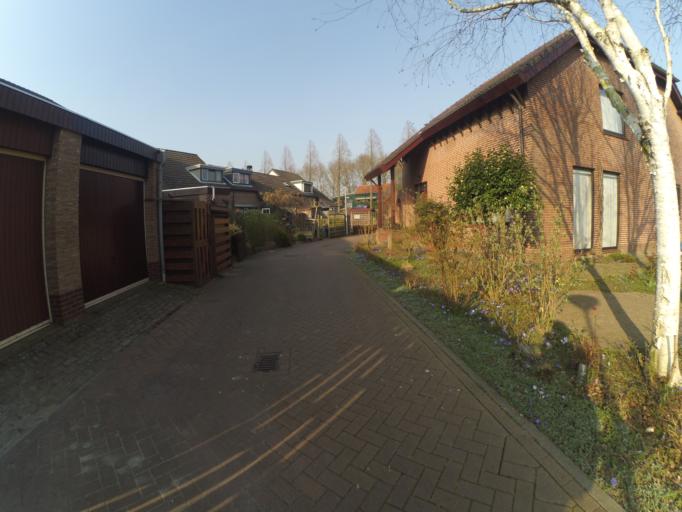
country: NL
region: South Holland
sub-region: Gemeente Spijkenisse
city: Spijkenisse
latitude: 51.8197
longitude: 4.2648
